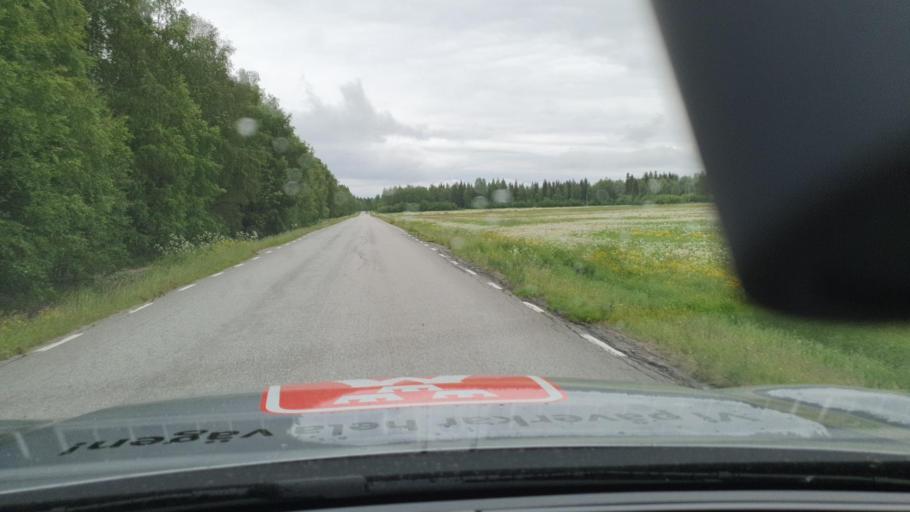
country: SE
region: Norrbotten
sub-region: Kalix Kommun
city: Toere
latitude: 65.8769
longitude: 22.6697
